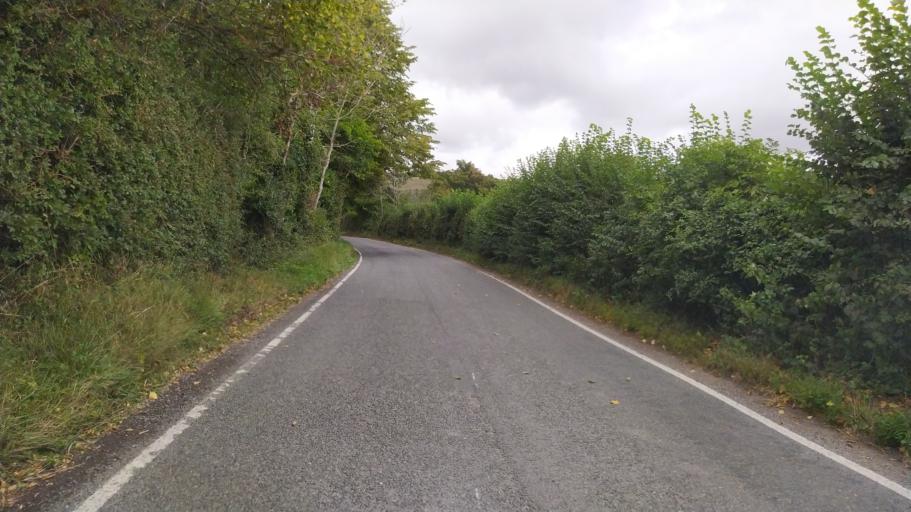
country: GB
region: England
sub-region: Hampshire
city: Petersfield
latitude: 50.9892
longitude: -1.0265
